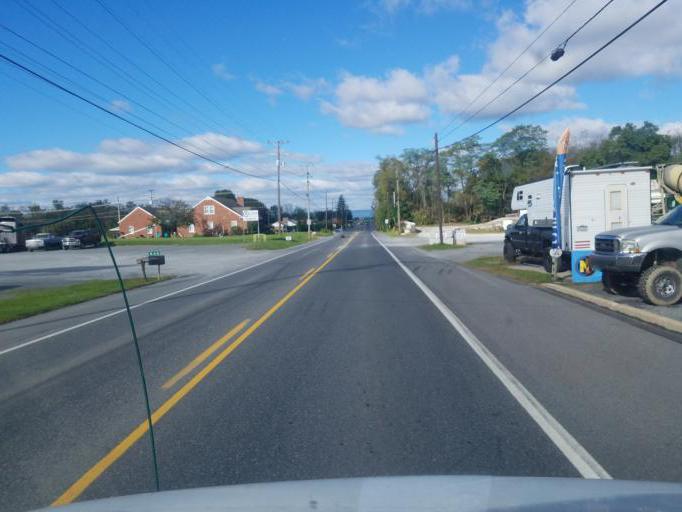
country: US
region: Pennsylvania
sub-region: Franklin County
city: Greencastle
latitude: 39.7847
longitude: -77.7032
